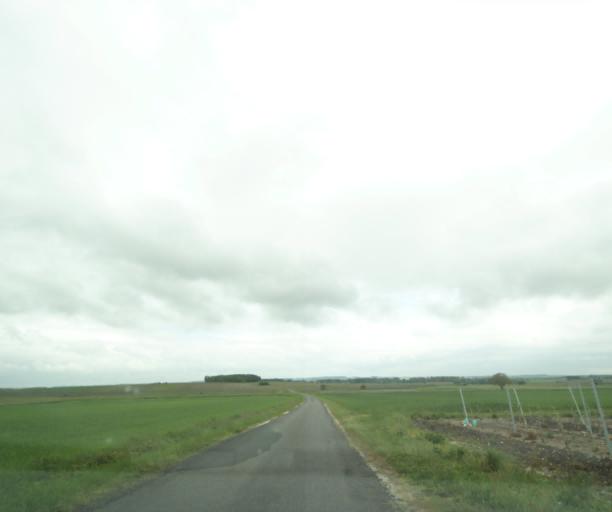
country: FR
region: Poitou-Charentes
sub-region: Departement de la Charente-Maritime
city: Perignac
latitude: 45.6665
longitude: -0.4995
